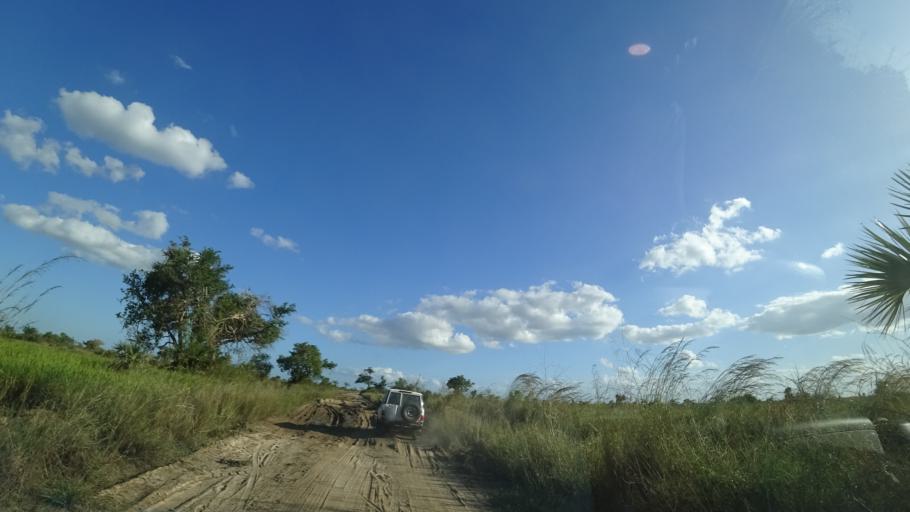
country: MZ
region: Sofala
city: Dondo
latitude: -19.4027
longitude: 34.5674
